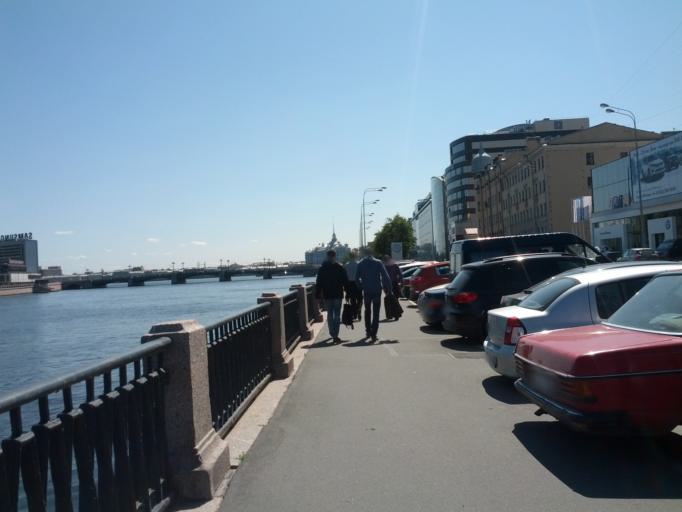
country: RU
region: St.-Petersburg
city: Petrogradka
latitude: 59.9622
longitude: 30.3348
